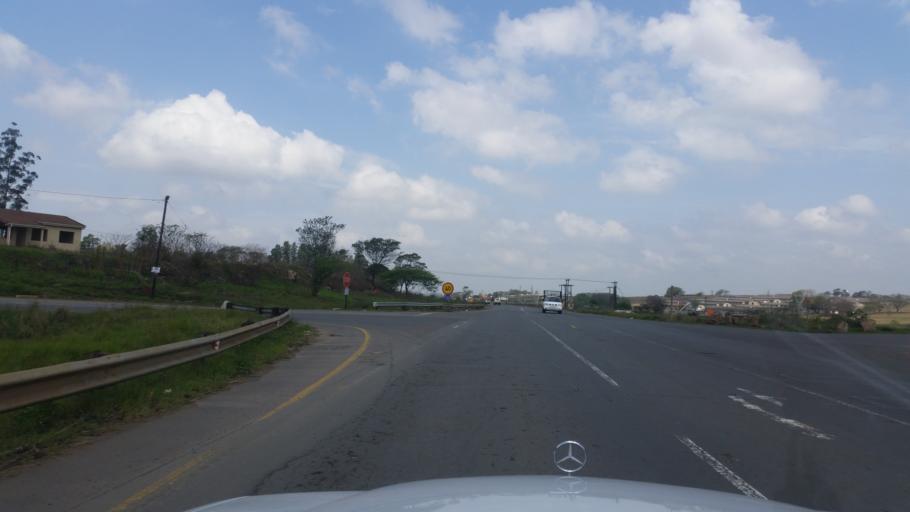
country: ZA
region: KwaZulu-Natal
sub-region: uMgungundlovu District Municipality
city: Camperdown
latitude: -29.7250
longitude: 30.4995
